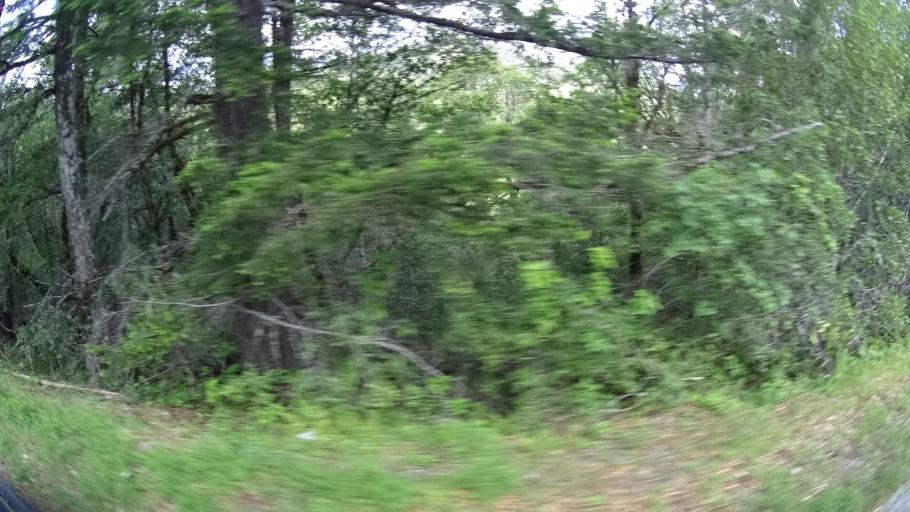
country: US
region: California
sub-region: Humboldt County
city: Redway
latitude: 40.0913
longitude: -123.8058
